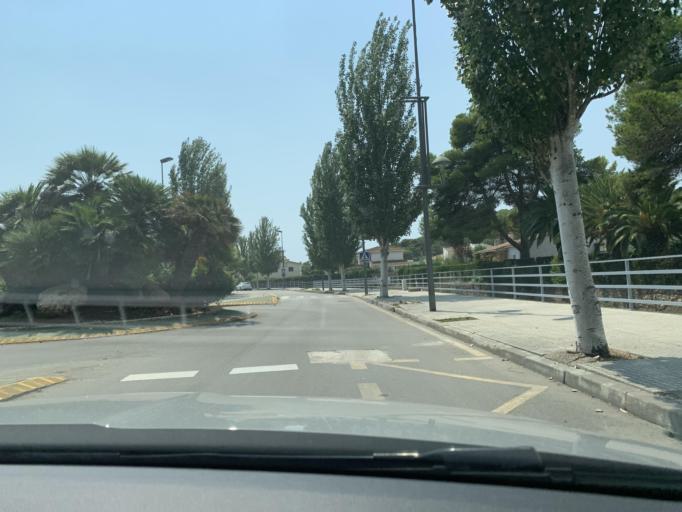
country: ES
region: Catalonia
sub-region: Provincia de Tarragona
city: Altafulla
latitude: 41.1316
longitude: 1.3451
